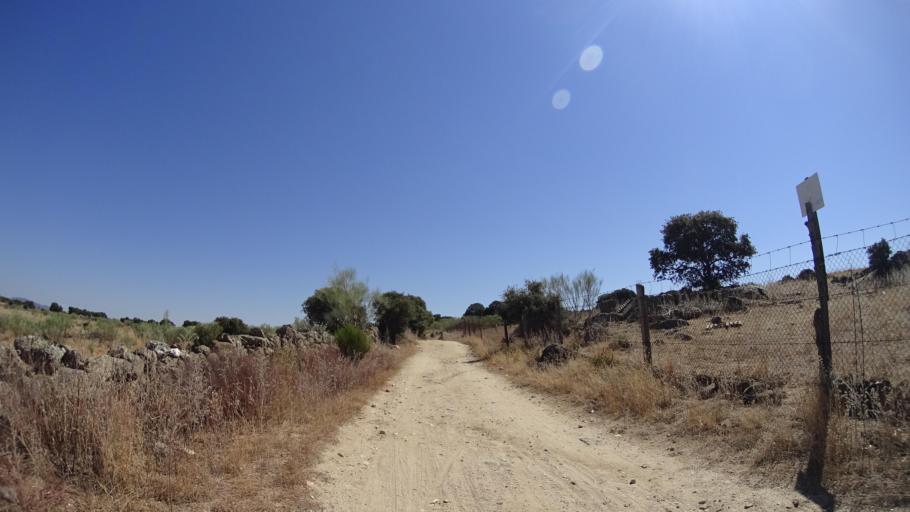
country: ES
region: Madrid
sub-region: Provincia de Madrid
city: Colmenarejo
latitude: 40.5223
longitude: -4.0126
